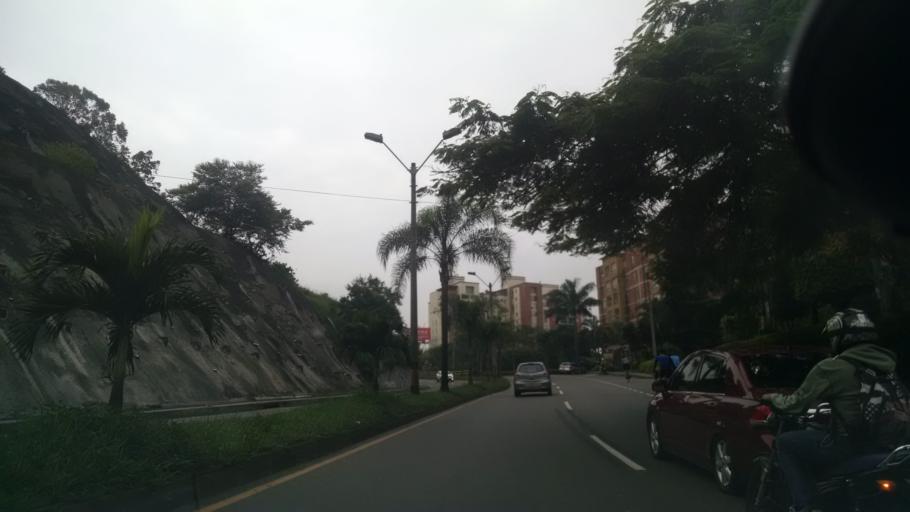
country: CO
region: Antioquia
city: Medellin
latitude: 6.2306
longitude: -75.5660
